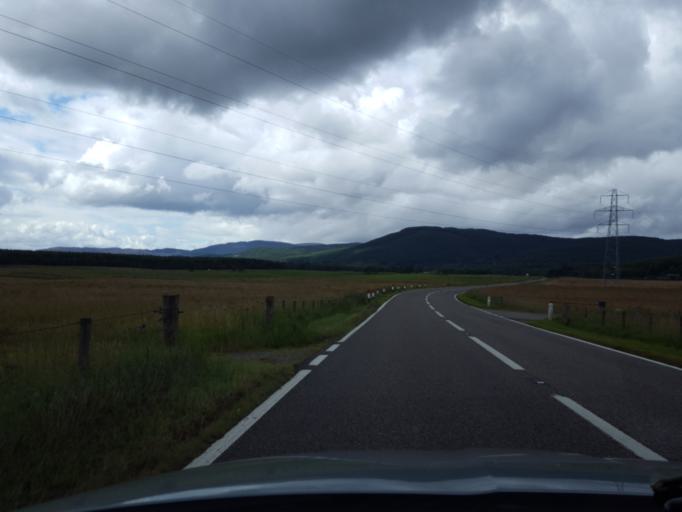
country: GB
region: Scotland
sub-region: Highland
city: Aviemore
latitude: 57.2563
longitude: -3.7625
